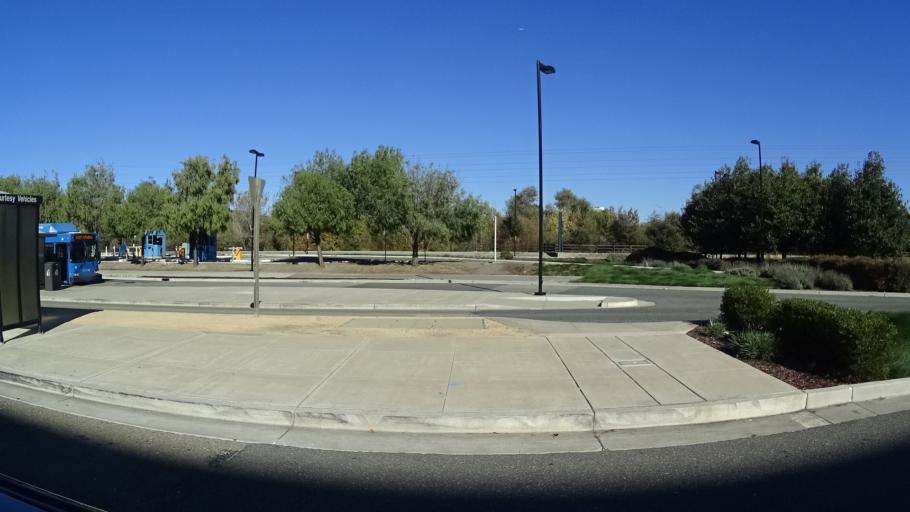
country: US
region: California
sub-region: Santa Clara County
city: Santa Clara
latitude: 37.3679
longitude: -121.9272
